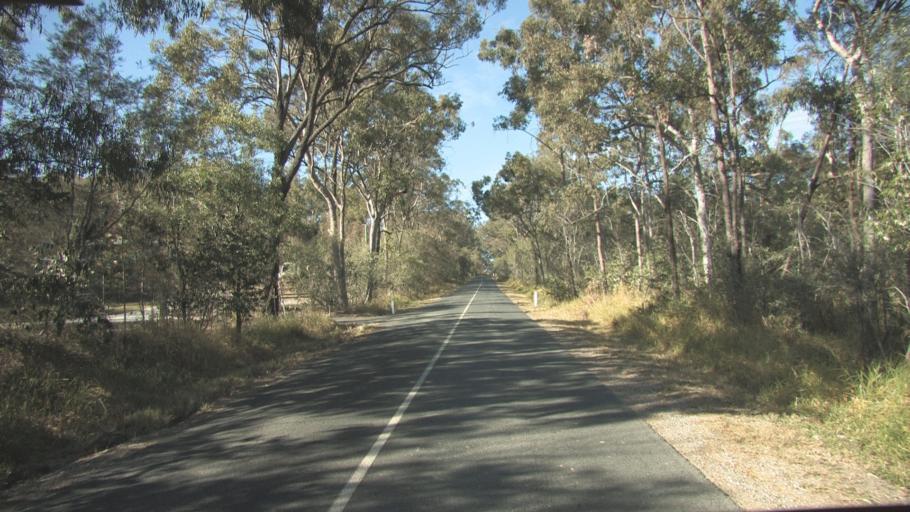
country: AU
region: Queensland
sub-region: Logan
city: Windaroo
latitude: -27.8146
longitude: 153.1676
